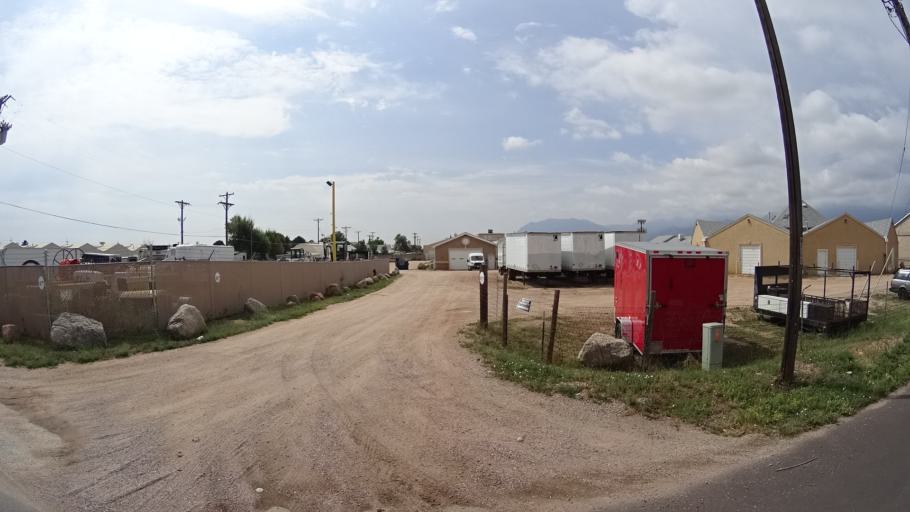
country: US
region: Colorado
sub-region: El Paso County
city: Colorado Springs
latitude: 38.8793
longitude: -104.8210
